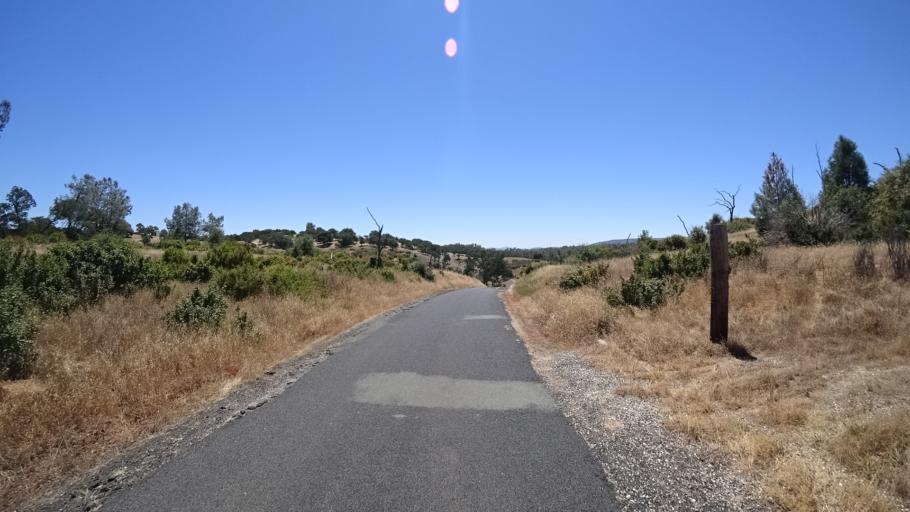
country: US
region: California
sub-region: Calaveras County
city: Copperopolis
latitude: 37.9820
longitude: -120.6962
